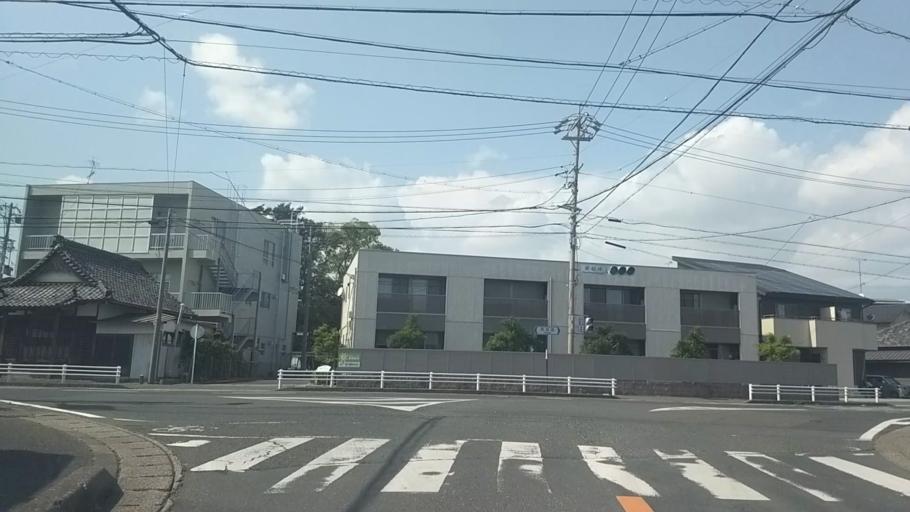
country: JP
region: Shizuoka
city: Hamamatsu
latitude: 34.6877
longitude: 137.7121
